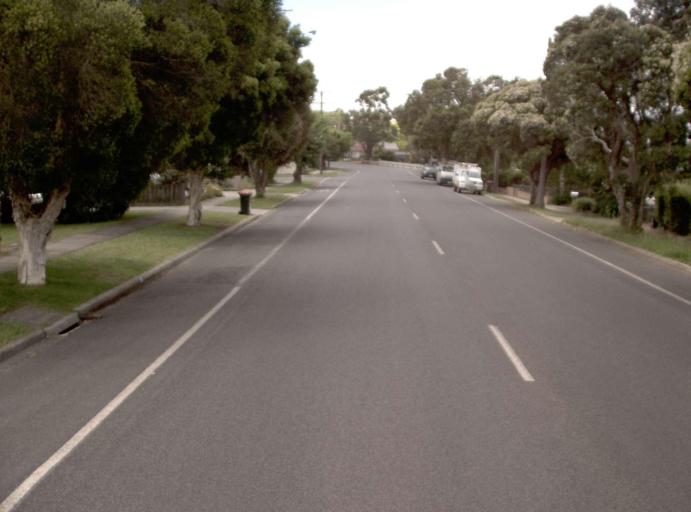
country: AU
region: Victoria
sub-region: Baw Baw
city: Warragul
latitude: -38.1450
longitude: 145.9380
